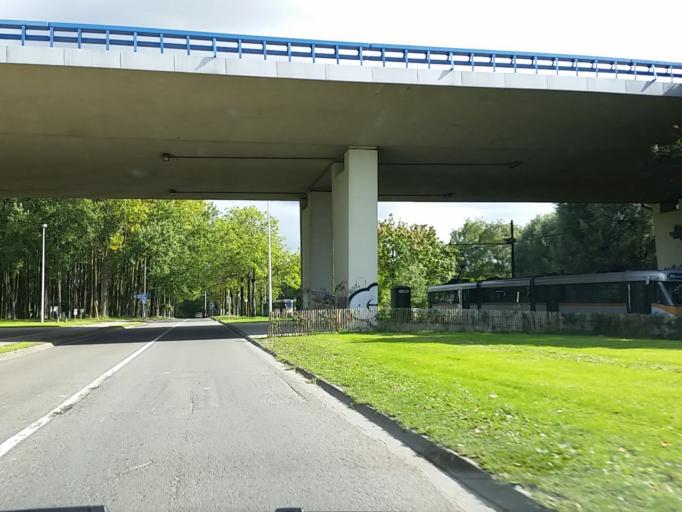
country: BE
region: Flanders
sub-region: Provincie Vlaams-Brabant
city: Dilbeek
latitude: 50.8250
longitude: 4.2798
